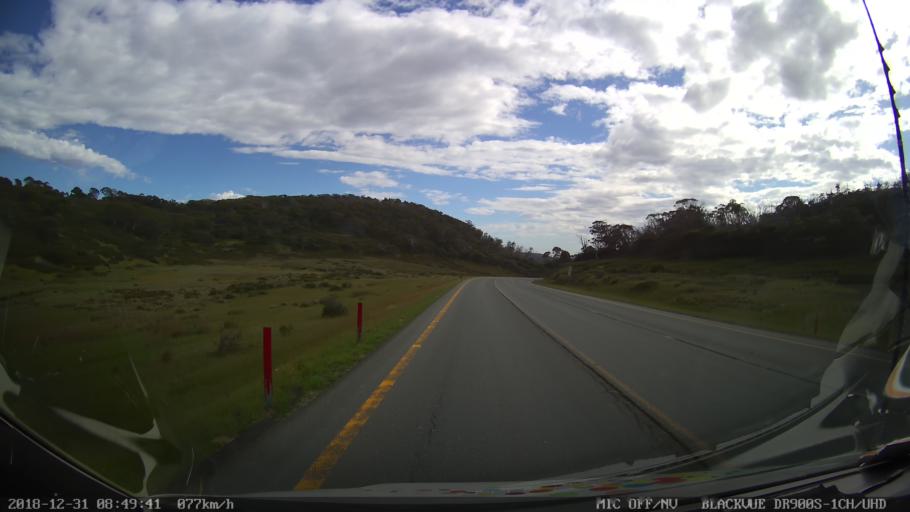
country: AU
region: New South Wales
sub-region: Snowy River
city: Jindabyne
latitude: -36.3596
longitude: 148.5096
